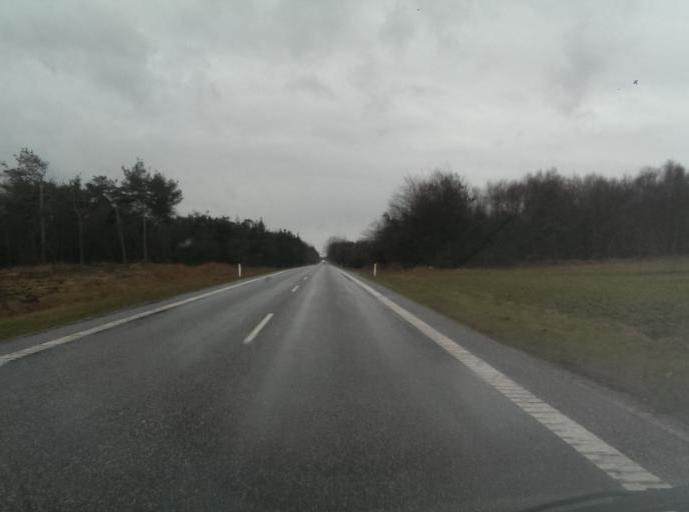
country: DK
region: Central Jutland
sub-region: Ringkobing-Skjern Kommune
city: Tarm
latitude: 55.8549
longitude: 8.4970
